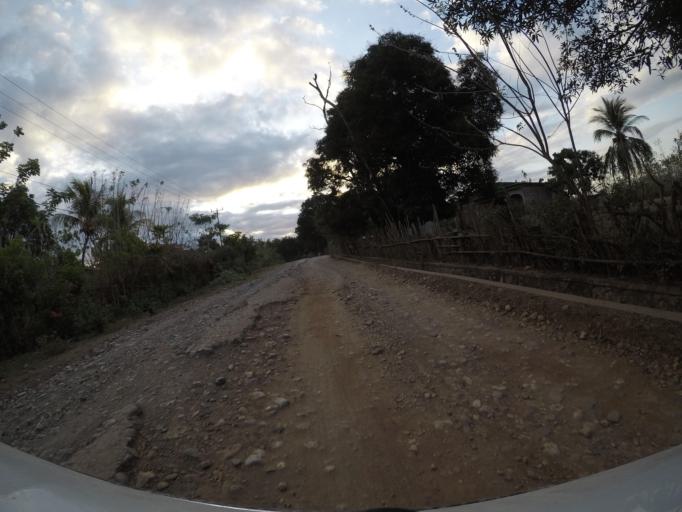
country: TL
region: Bobonaro
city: Maliana
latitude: -8.9233
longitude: 125.2107
